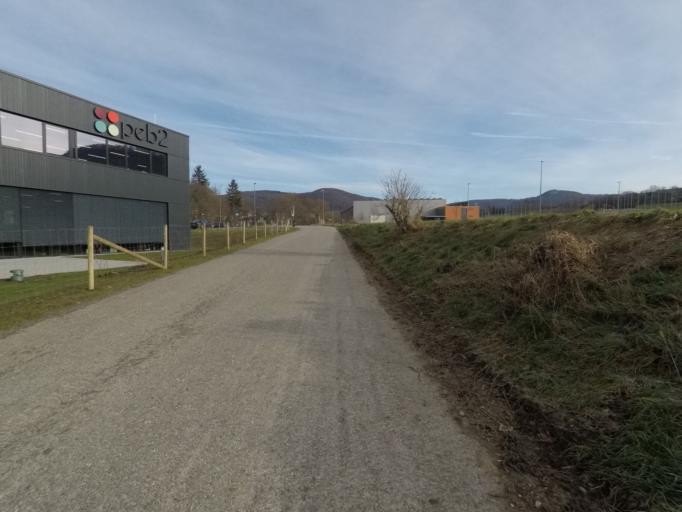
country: DE
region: Baden-Wuerttemberg
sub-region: Tuebingen Region
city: Pfullingen
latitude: 48.4767
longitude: 9.2418
